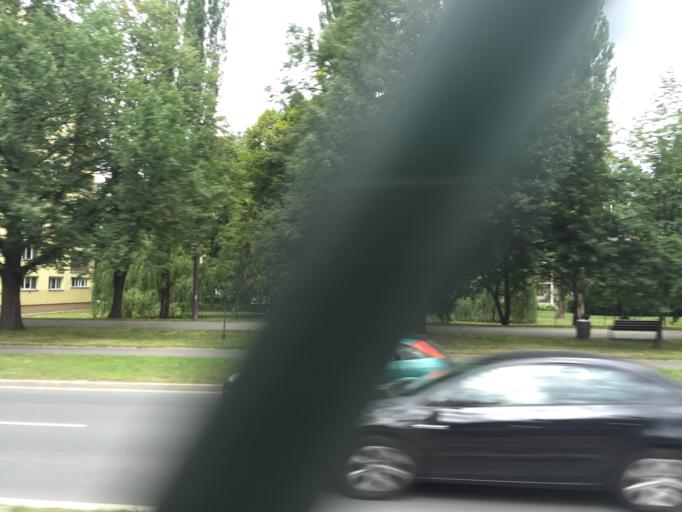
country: PL
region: Lesser Poland Voivodeship
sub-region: Powiat wielicki
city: Czarnochowice
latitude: 50.0731
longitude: 20.0221
